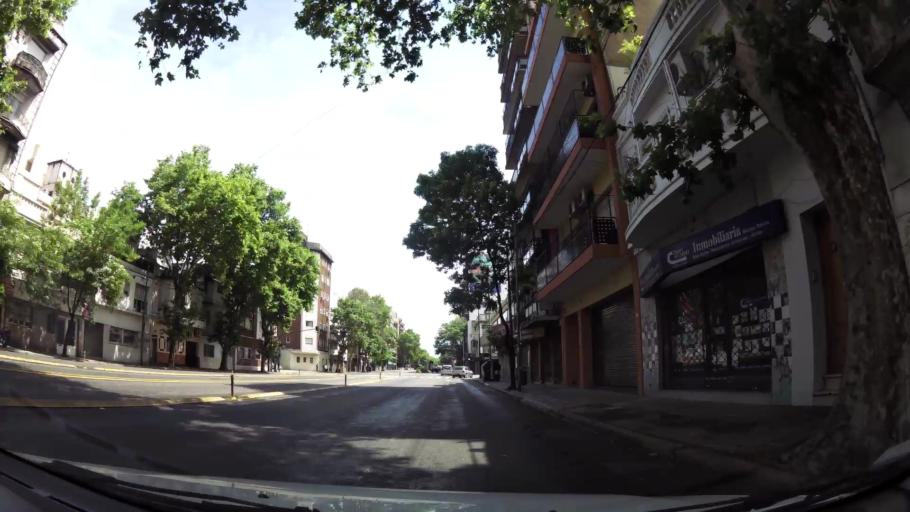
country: AR
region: Buenos Aires F.D.
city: Villa Santa Rita
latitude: -34.6034
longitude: -58.4570
